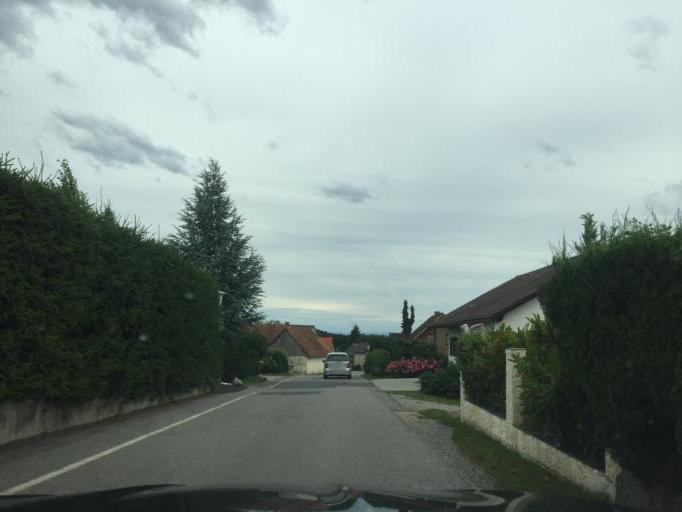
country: AT
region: Styria
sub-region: Politischer Bezirk Graz-Umgebung
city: Hart bei Graz
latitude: 47.0581
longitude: 15.5136
